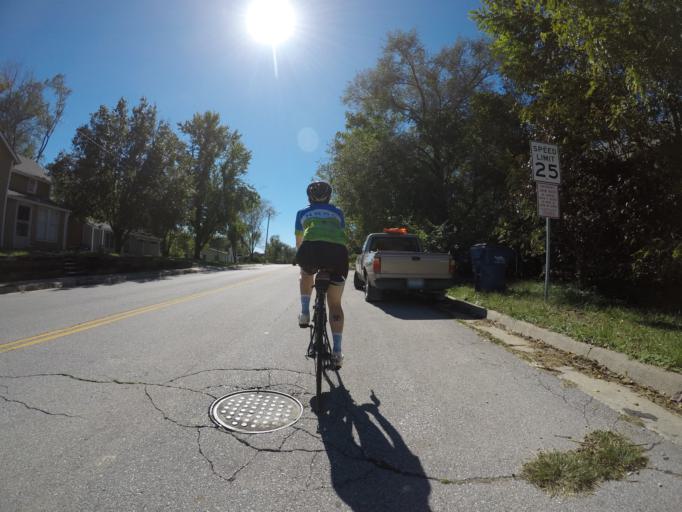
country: US
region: Kansas
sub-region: Johnson County
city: De Soto
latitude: 38.9805
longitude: -94.9651
